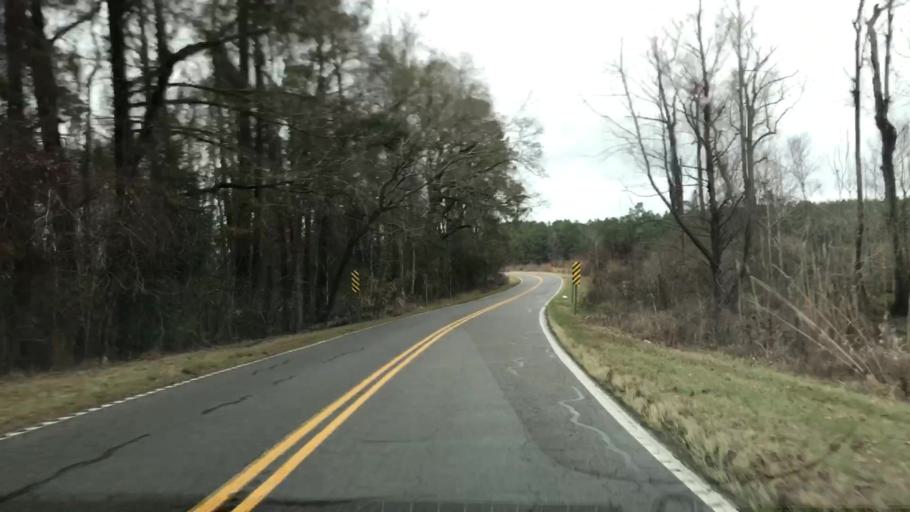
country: US
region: South Carolina
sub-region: Florence County
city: Johnsonville
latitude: 33.6571
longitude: -79.3045
